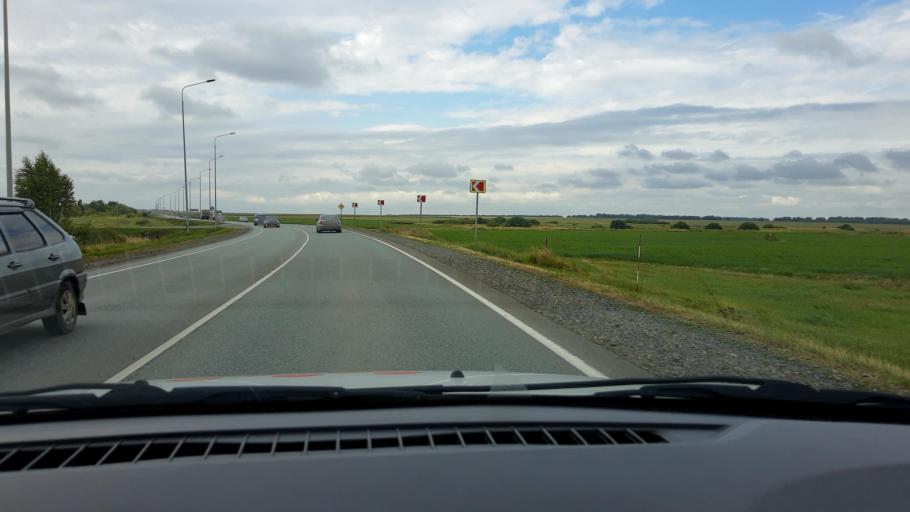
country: RU
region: Tatarstan
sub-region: Alekseyevskiy Rayon
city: Alekseyevskoye
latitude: 55.3122
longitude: 50.2945
